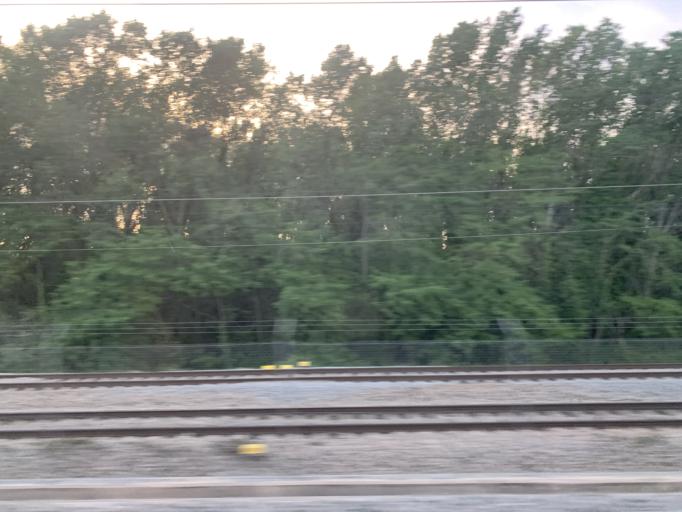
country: ES
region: Catalonia
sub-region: Provincia de Barcelona
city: Llinars del Valles
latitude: 41.6492
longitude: 2.4216
